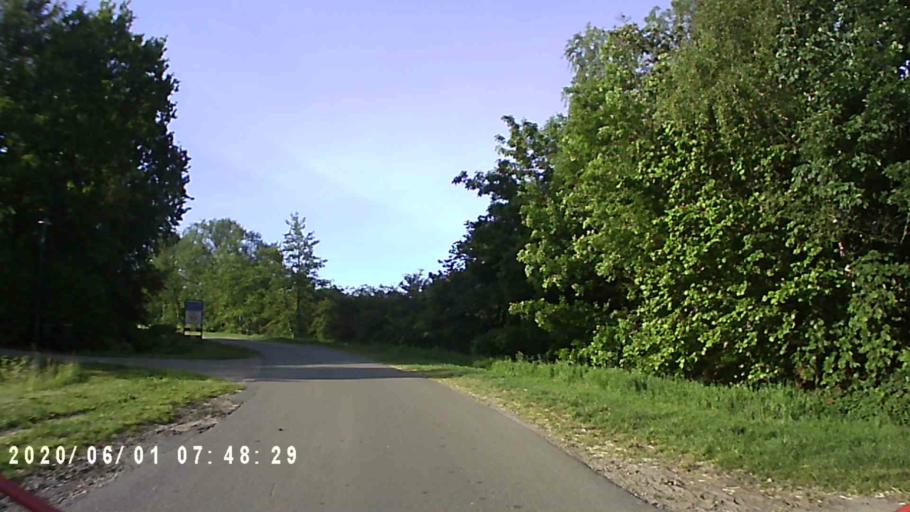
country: NL
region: Friesland
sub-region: Gemeente Dantumadiel
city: Rinsumageast
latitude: 53.2950
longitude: 5.9521
